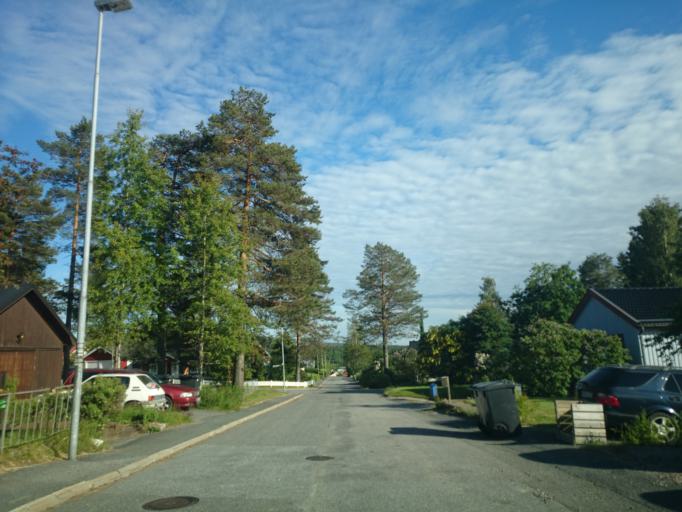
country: SE
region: Vaesternorrland
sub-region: Haernoesands Kommun
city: Haernoesand
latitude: 62.6473
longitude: 17.8936
